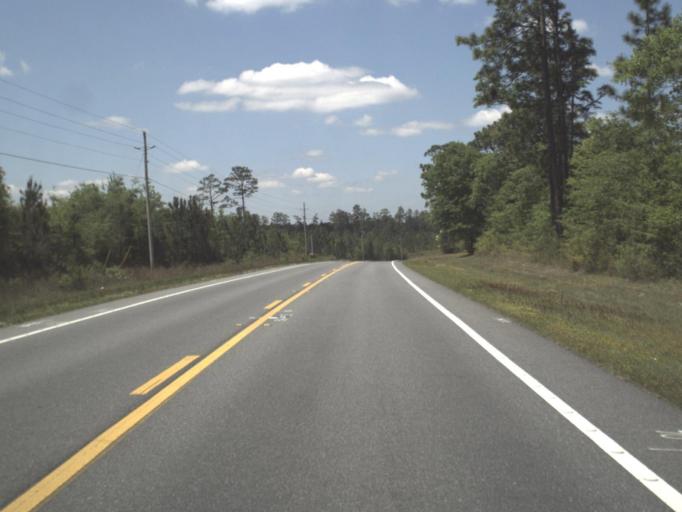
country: US
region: Alabama
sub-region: Escambia County
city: East Brewton
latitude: 30.9561
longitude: -87.0424
